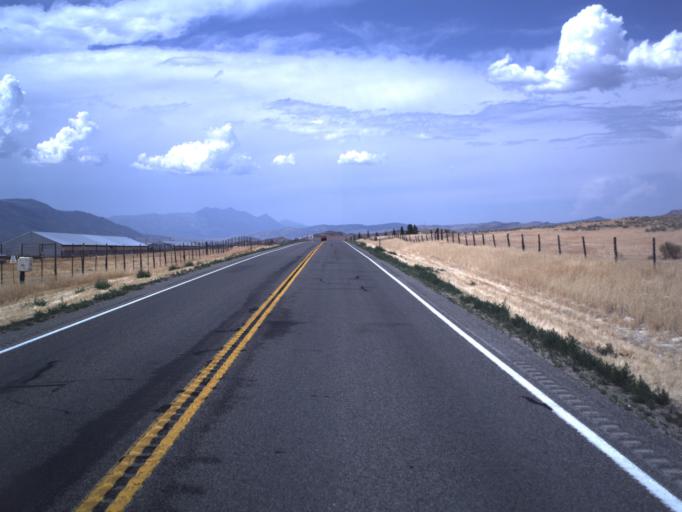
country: US
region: Utah
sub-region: Sanpete County
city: Moroni
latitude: 39.4963
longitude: -111.5640
